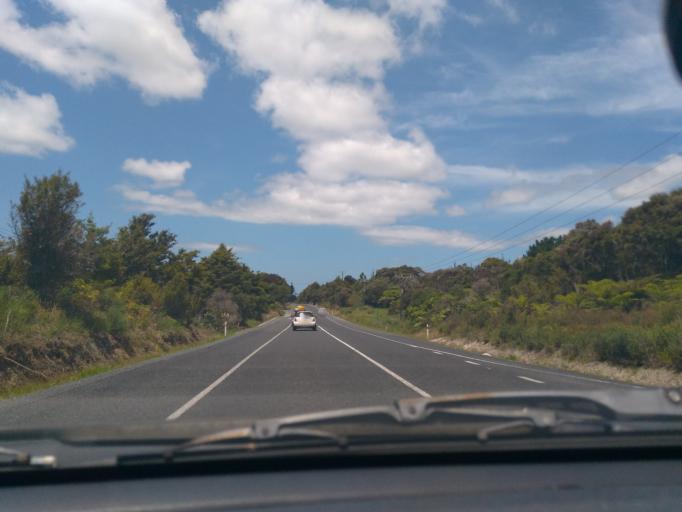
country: NZ
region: Northland
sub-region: Far North District
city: Kerikeri
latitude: -35.1213
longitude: 173.8622
